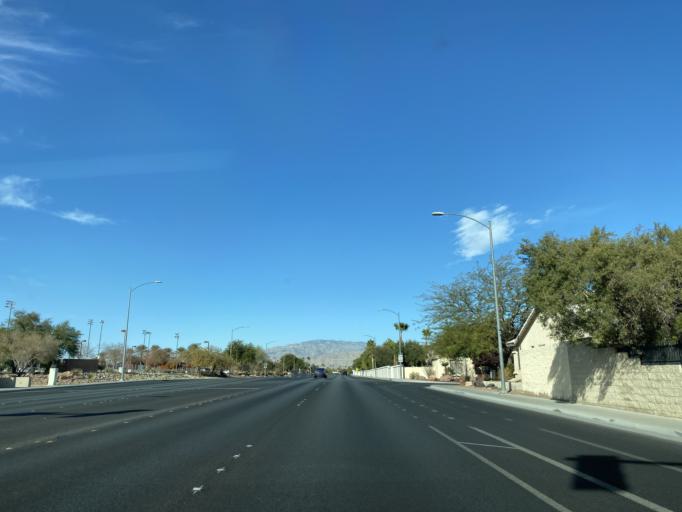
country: US
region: Nevada
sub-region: Clark County
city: Las Vegas
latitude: 36.2867
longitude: -115.2603
